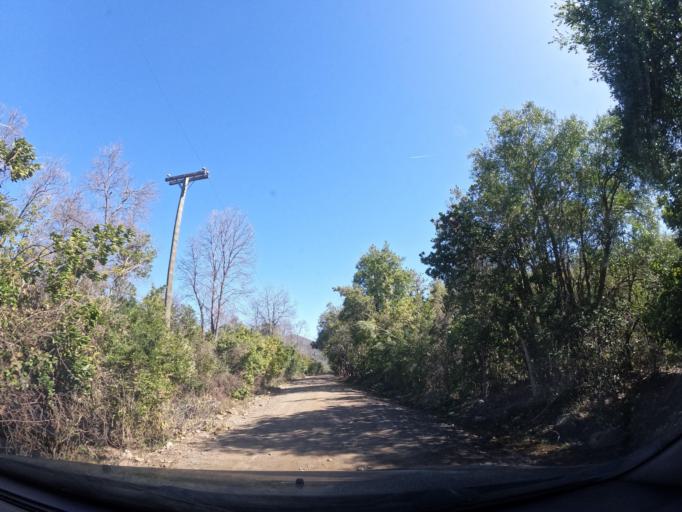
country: CL
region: Maule
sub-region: Provincia de Linares
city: Longavi
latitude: -36.2471
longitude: -71.3362
